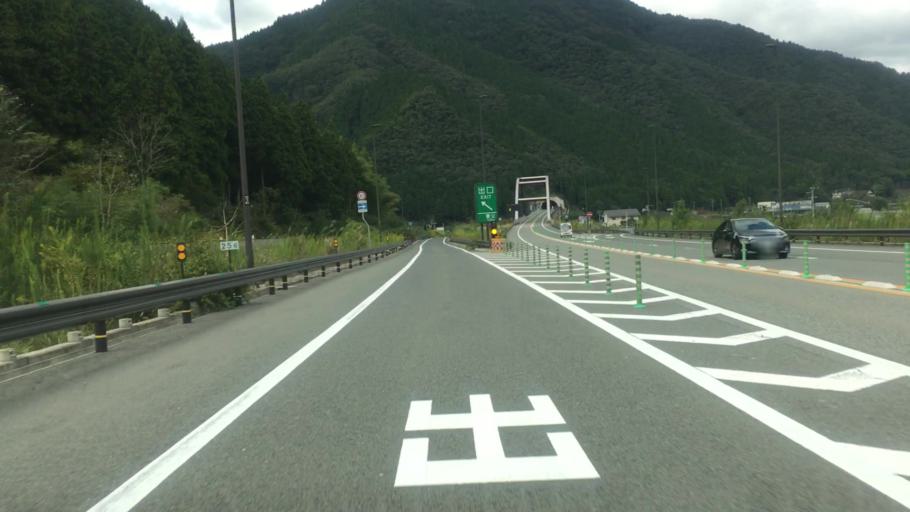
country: JP
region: Hyogo
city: Toyooka
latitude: 35.3579
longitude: 134.7628
